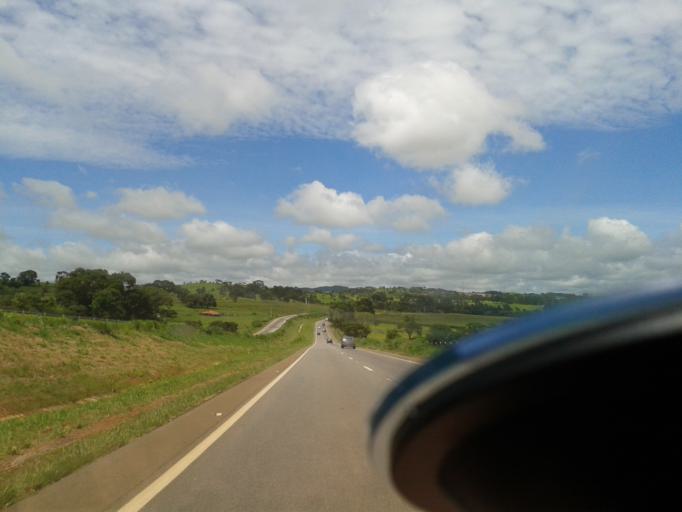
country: BR
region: Goias
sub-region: Inhumas
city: Inhumas
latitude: -16.2165
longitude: -49.5727
